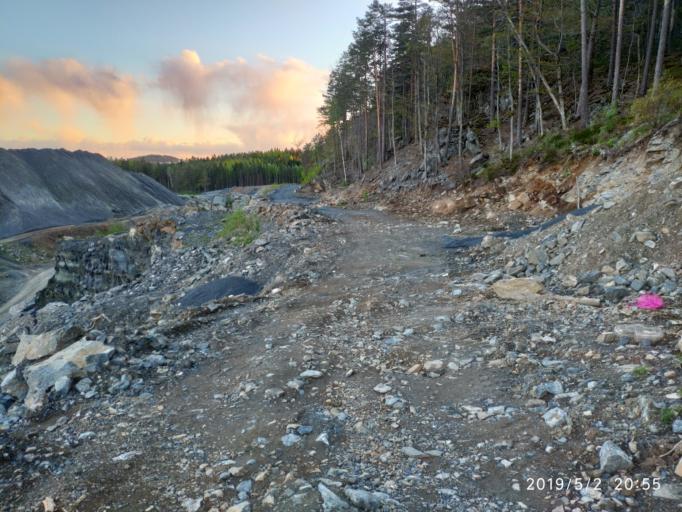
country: NO
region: Telemark
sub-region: Kragero
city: Kragero
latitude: 58.8881
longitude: 9.4197
